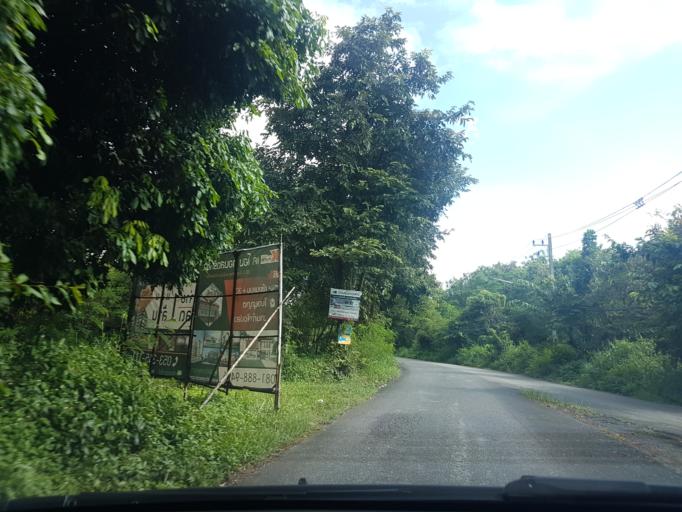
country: TH
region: Chiang Mai
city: San Sai
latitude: 18.8364
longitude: 99.0103
